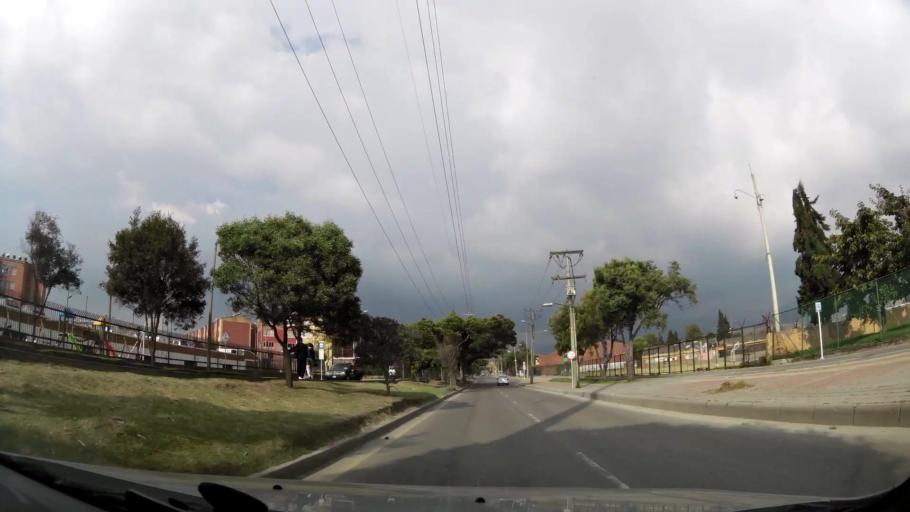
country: CO
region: Bogota D.C.
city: Bogota
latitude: 4.5752
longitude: -74.1344
